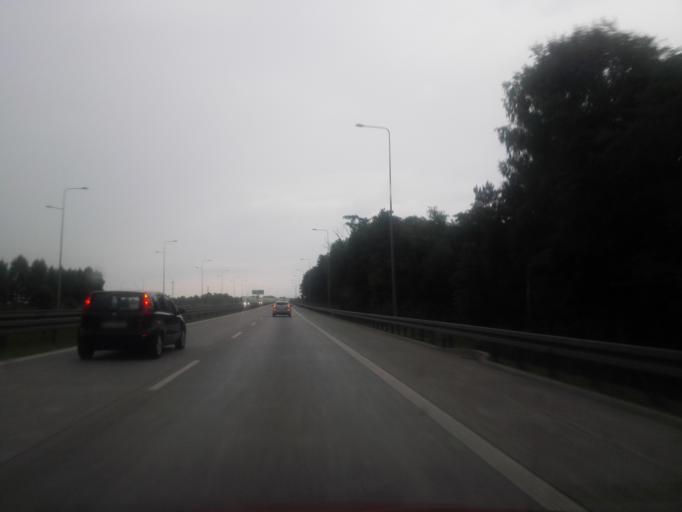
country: PL
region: Lodz Voivodeship
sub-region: Powiat piotrkowski
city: Wolborz
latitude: 51.4889
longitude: 19.8251
